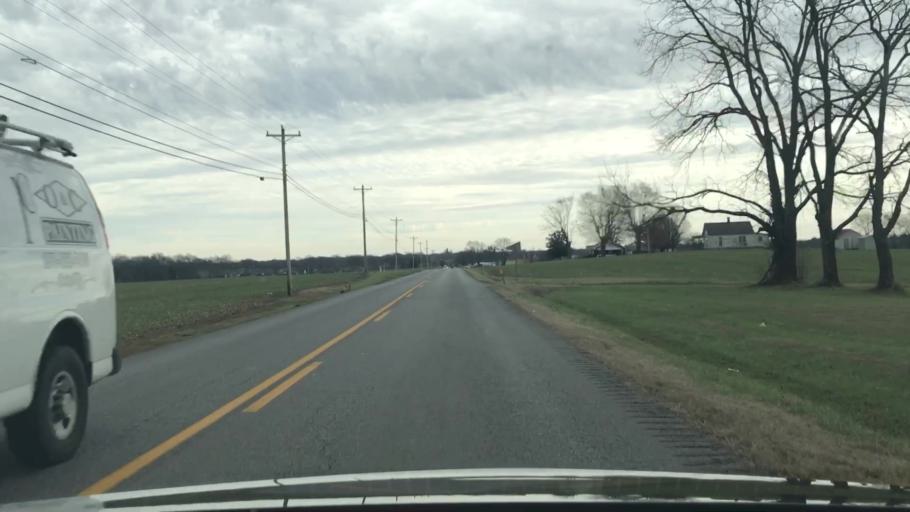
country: US
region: Kentucky
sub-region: Christian County
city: Hopkinsville
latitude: 36.8621
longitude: -87.5345
